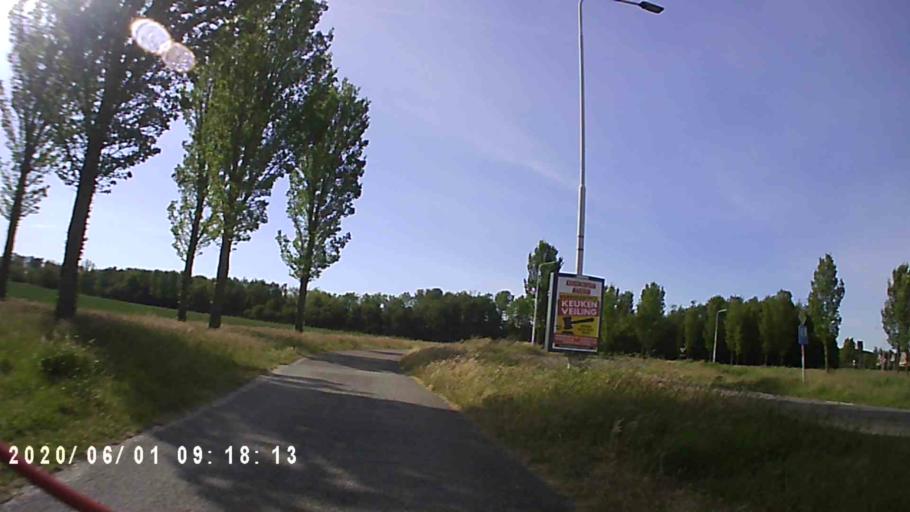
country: NL
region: Friesland
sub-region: Gemeente Leeuwarderadeel
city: Stiens
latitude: 53.2702
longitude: 5.7606
